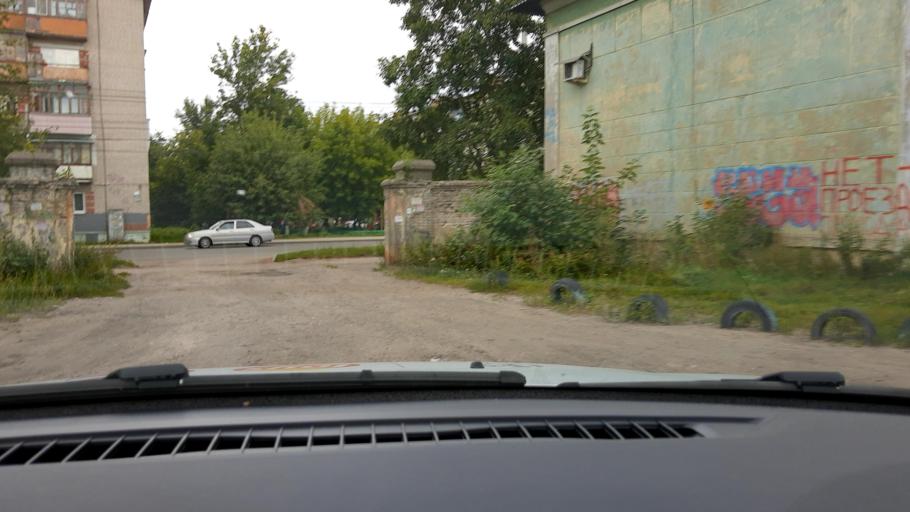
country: RU
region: Nizjnij Novgorod
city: Dzerzhinsk
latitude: 56.2359
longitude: 43.4820
